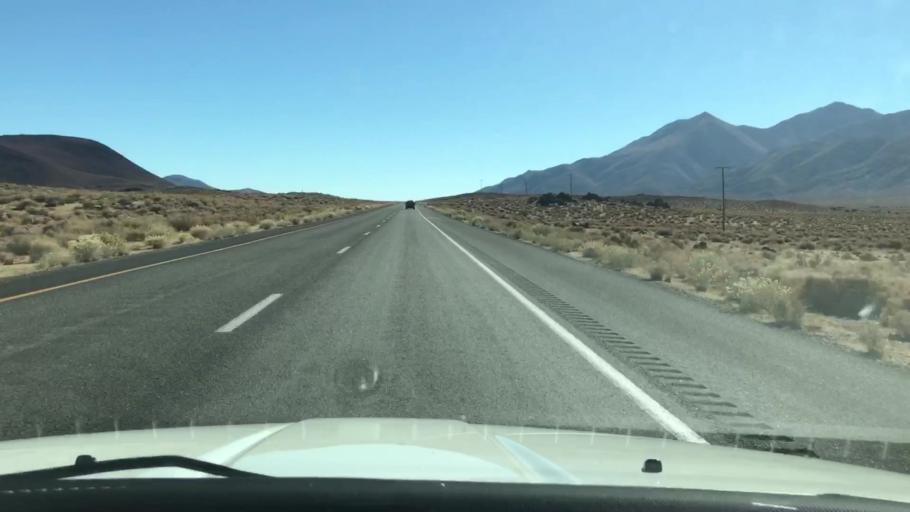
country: US
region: California
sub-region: Kern County
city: Inyokern
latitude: 36.0062
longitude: -117.9354
